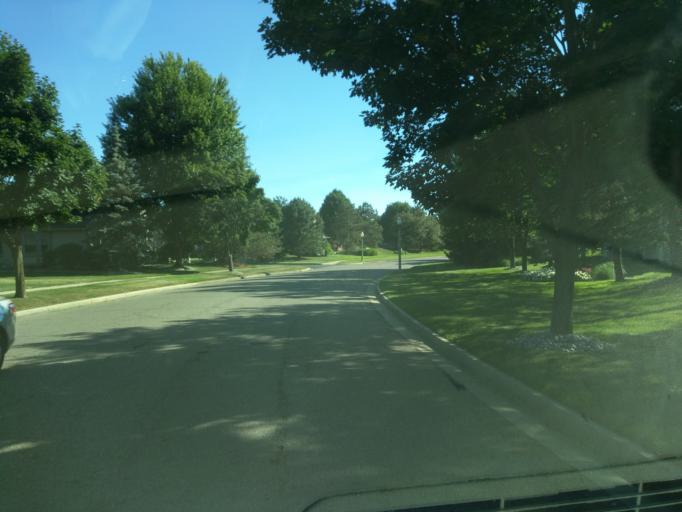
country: US
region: Michigan
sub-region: Eaton County
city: Waverly
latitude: 42.7322
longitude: -84.6352
